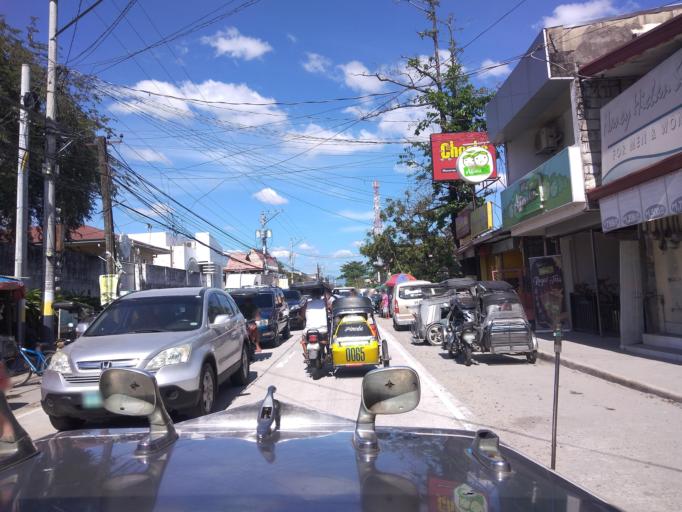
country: PH
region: Central Luzon
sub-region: Province of Pampanga
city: Santa Rita
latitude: 14.9978
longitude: 120.6143
